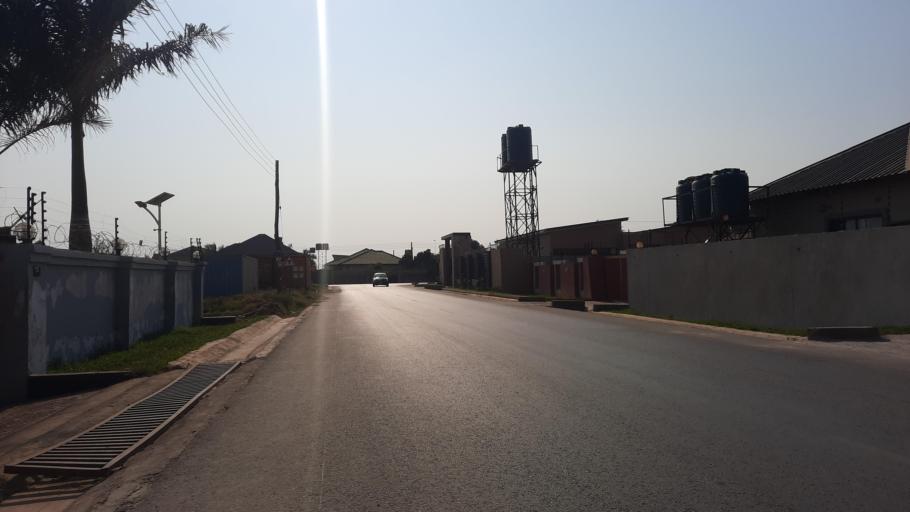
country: ZM
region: Lusaka
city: Lusaka
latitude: -15.3901
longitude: 28.3890
